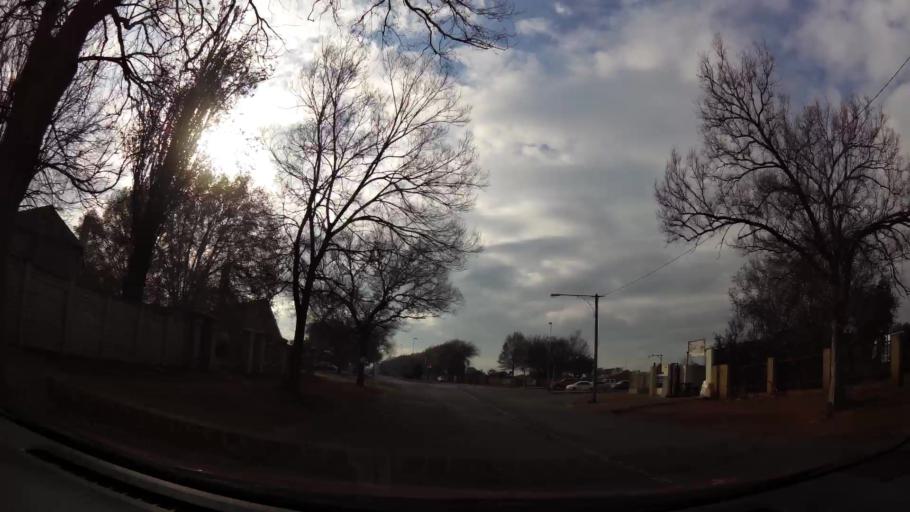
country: ZA
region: Gauteng
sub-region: Sedibeng District Municipality
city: Vanderbijlpark
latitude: -26.7057
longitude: 27.8235
